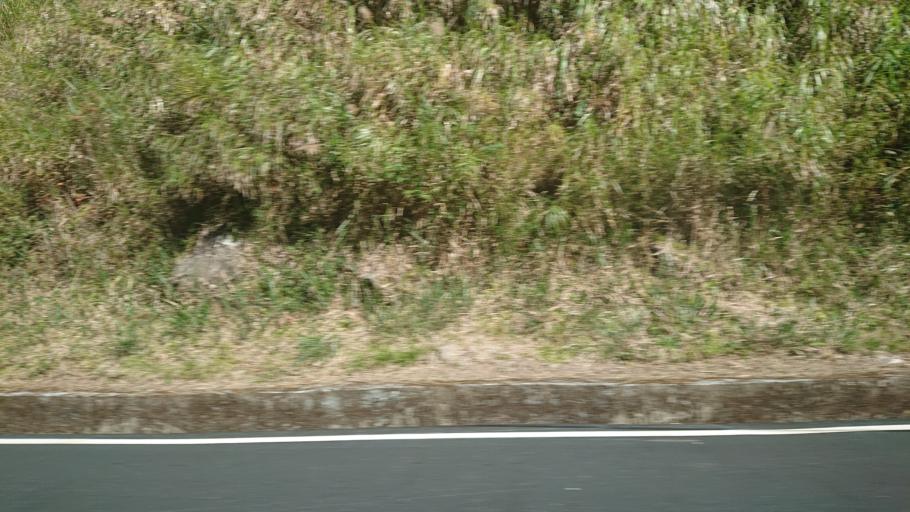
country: TW
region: Taiwan
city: Lugu
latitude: 23.4853
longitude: 120.8261
